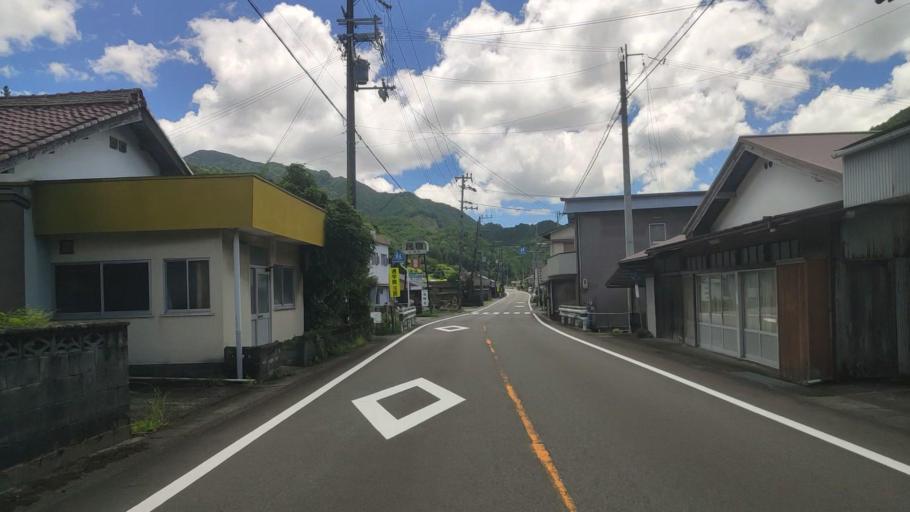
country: JP
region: Mie
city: Owase
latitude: 33.9773
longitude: 136.0534
